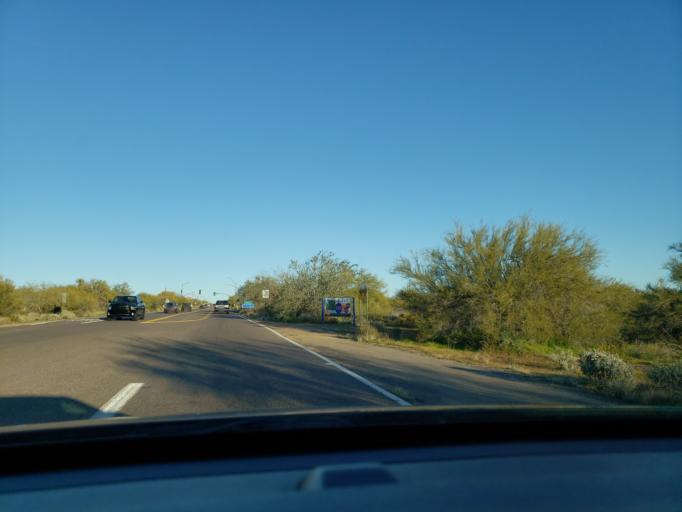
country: US
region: Arizona
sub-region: Maricopa County
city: Cave Creek
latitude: 33.7991
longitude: -111.9544
